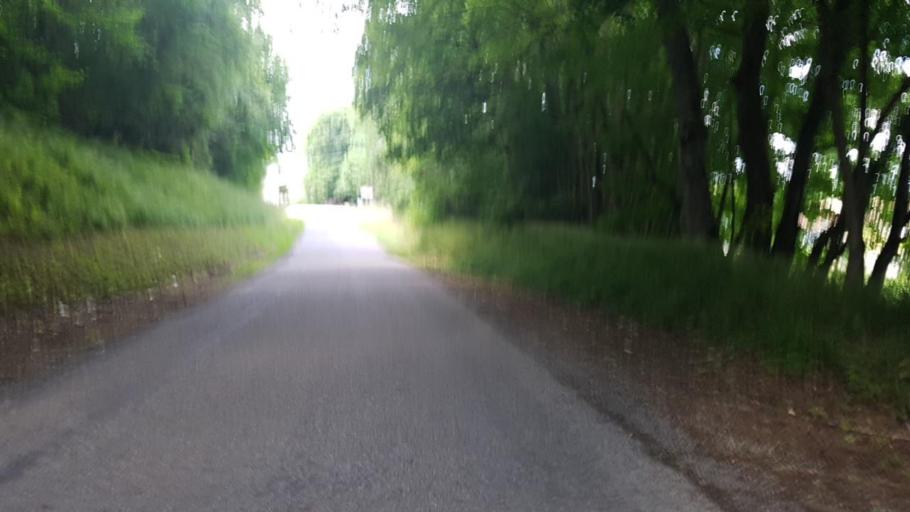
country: FR
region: Lorraine
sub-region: Departement de la Meuse
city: Vacon
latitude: 48.6873
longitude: 5.6260
